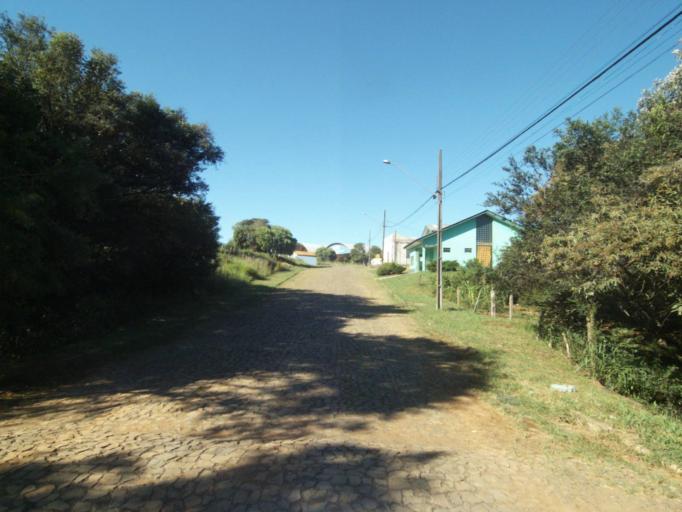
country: BR
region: Parana
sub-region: Pinhao
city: Pinhao
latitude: -25.8403
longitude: -52.0297
